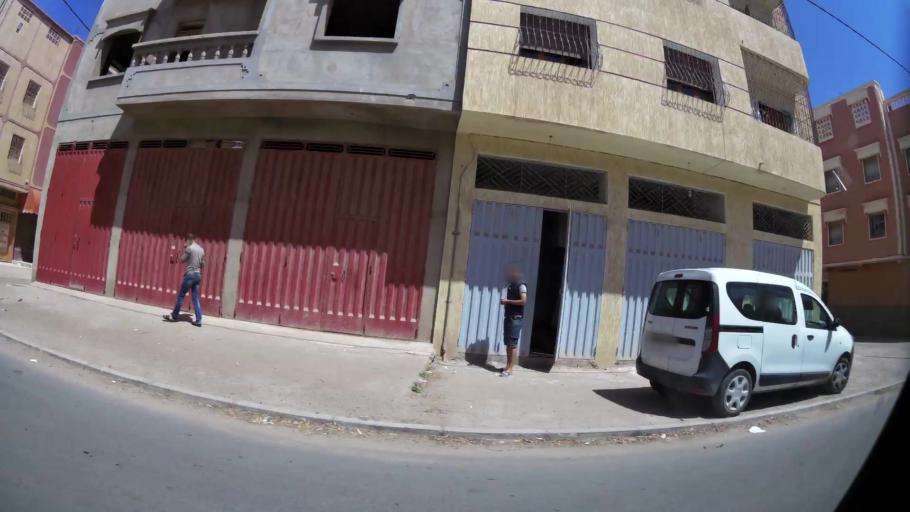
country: MA
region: Souss-Massa-Draa
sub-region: Inezgane-Ait Mellou
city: Inezgane
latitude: 30.3227
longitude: -9.5006
